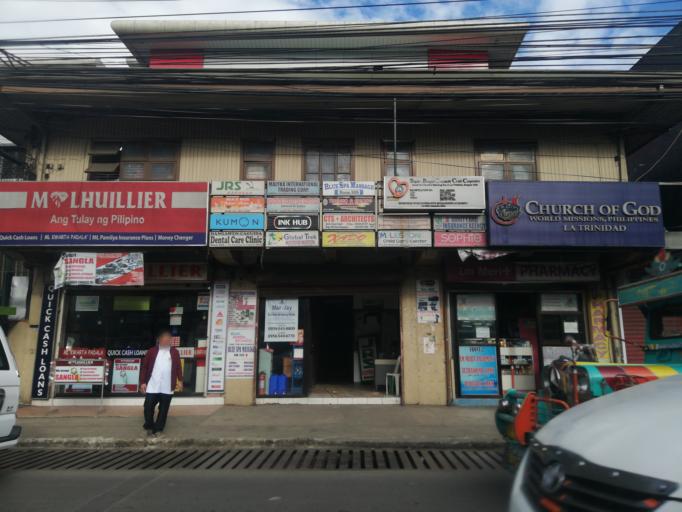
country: PH
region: Cordillera
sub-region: Province of Benguet
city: La Trinidad
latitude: 16.4465
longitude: 120.5912
